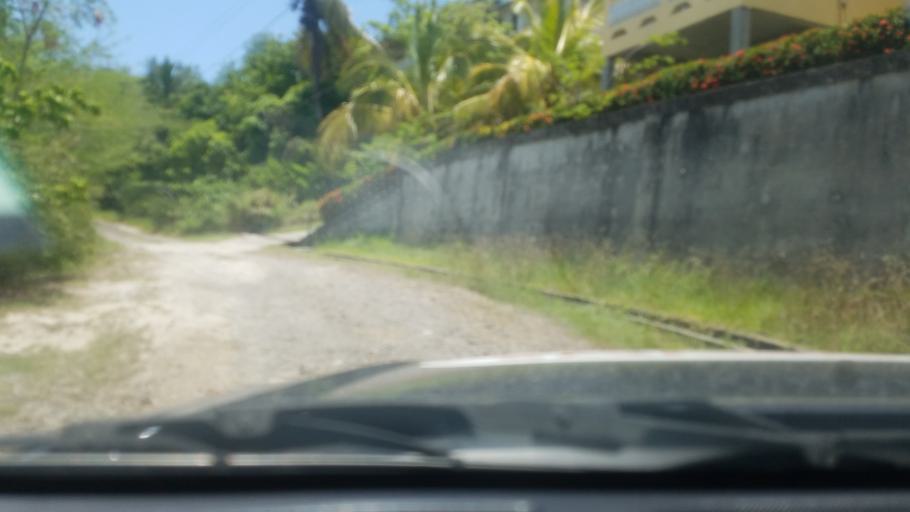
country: LC
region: Vieux-Fort
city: Vieux Fort
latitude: 13.7146
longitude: -60.9488
